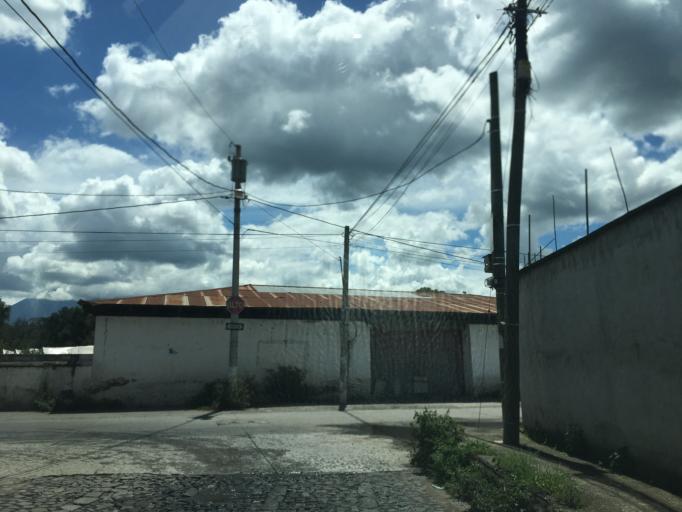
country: GT
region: Sacatepequez
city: Antigua Guatemala
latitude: 14.5455
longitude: -90.7328
